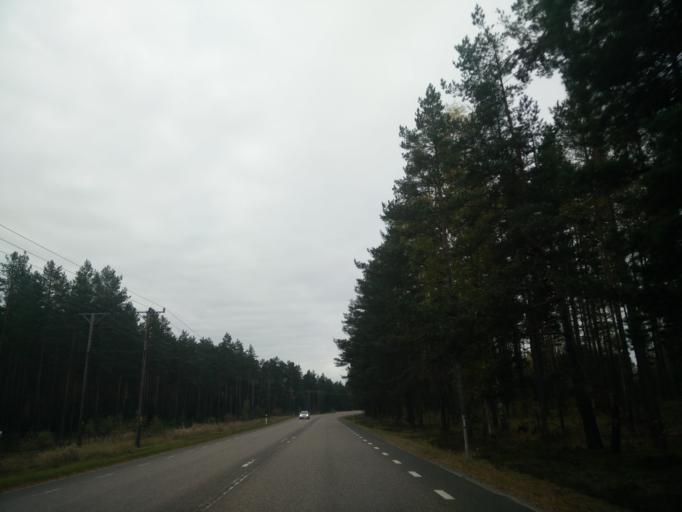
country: SE
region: Gaevleborg
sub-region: Gavle Kommun
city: Gavle
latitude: 60.7828
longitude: 17.2005
